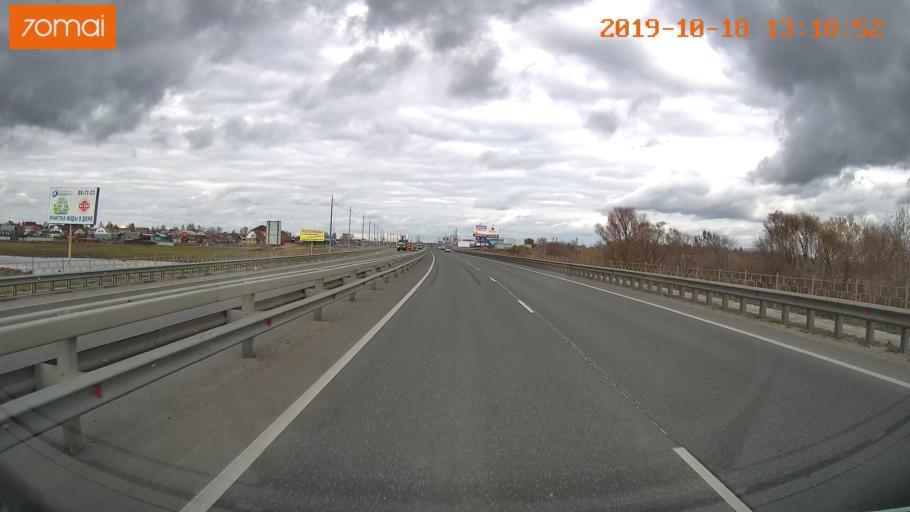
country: RU
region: Rjazan
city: Polyany
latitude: 54.6604
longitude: 39.8211
